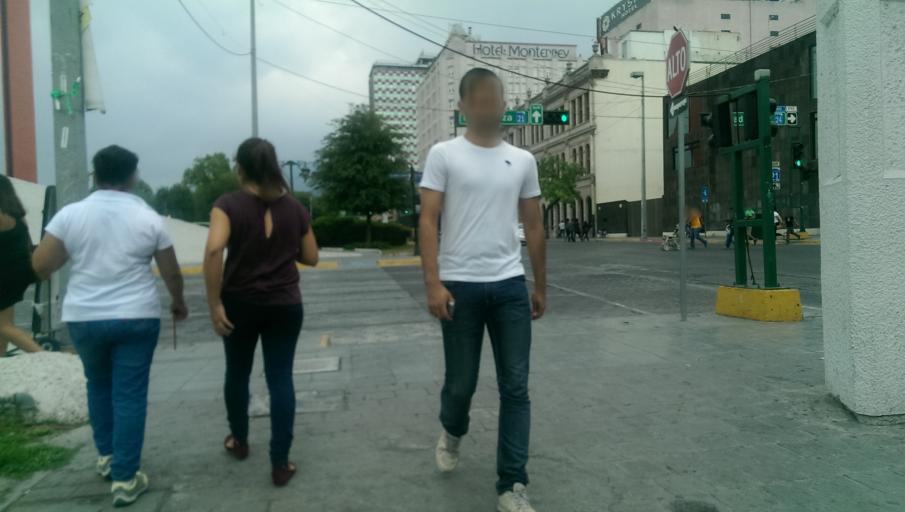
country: MX
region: Nuevo Leon
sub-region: Monterrey
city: Monterrey
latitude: 25.6680
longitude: -100.3104
